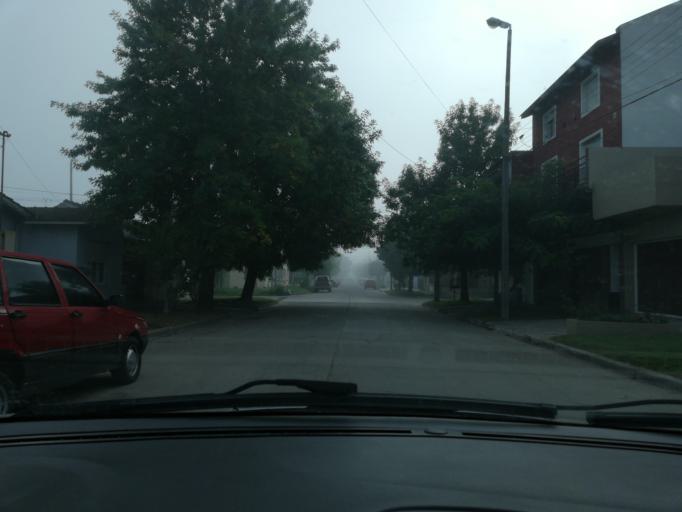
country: AR
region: Buenos Aires
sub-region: Partido de Balcarce
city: Balcarce
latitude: -37.8544
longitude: -58.2633
